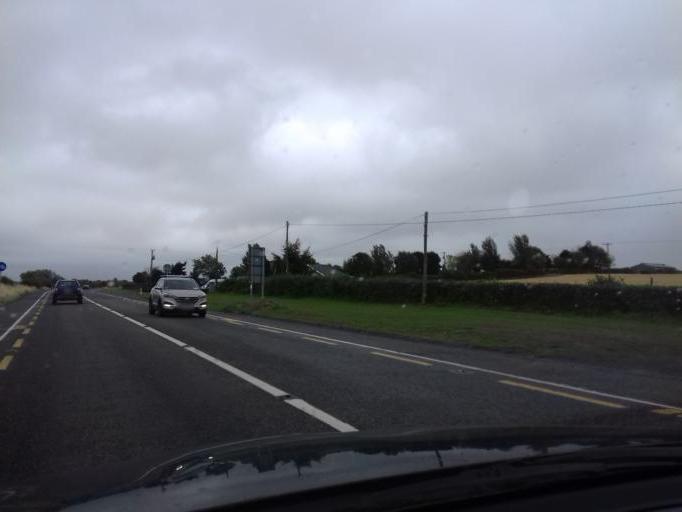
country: IE
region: Leinster
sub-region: County Carlow
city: Bagenalstown
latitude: 52.7471
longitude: -6.9675
